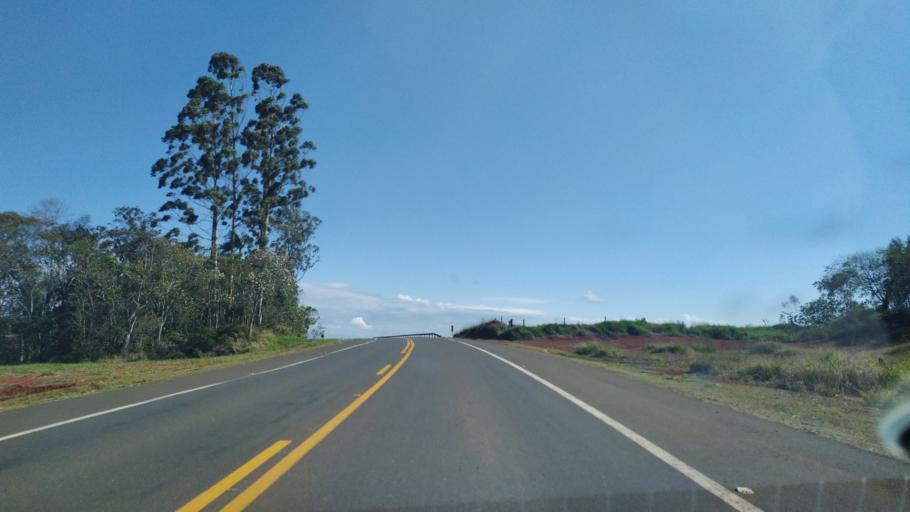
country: BR
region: Parana
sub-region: Ortigueira
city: Ortigueira
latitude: -24.2558
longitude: -50.8022
